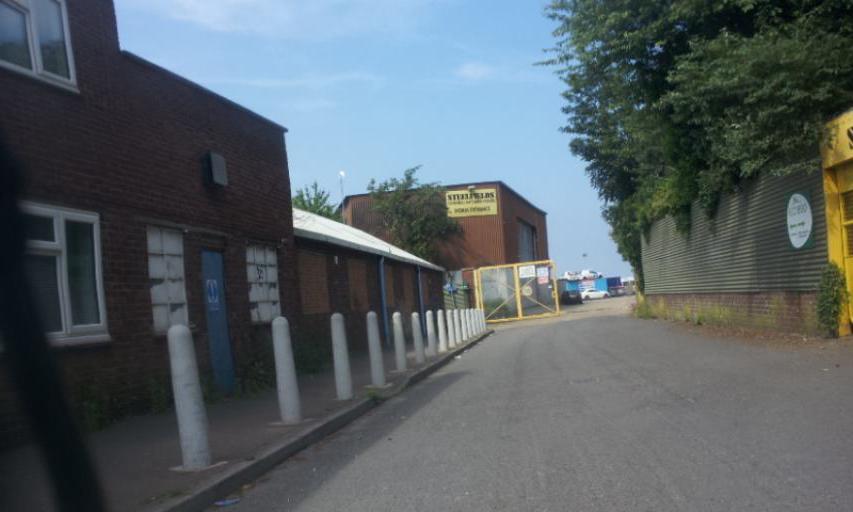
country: GB
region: England
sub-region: Kent
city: Gillingham
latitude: 51.3915
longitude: 0.5718
